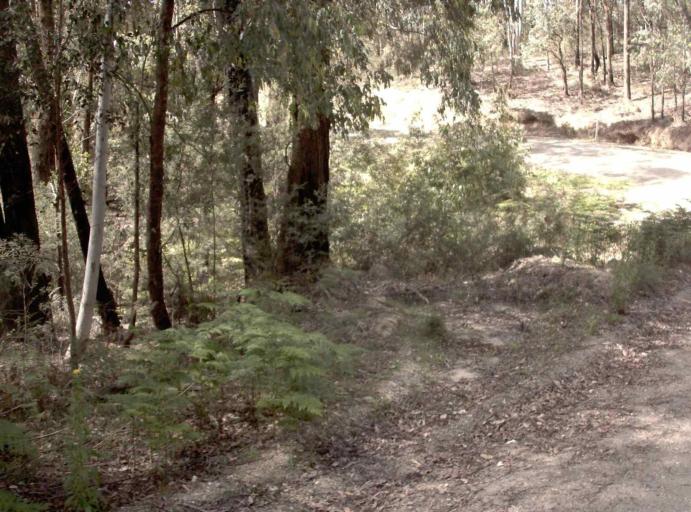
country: AU
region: New South Wales
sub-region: Bombala
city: Bombala
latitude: -37.1850
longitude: 148.7084
